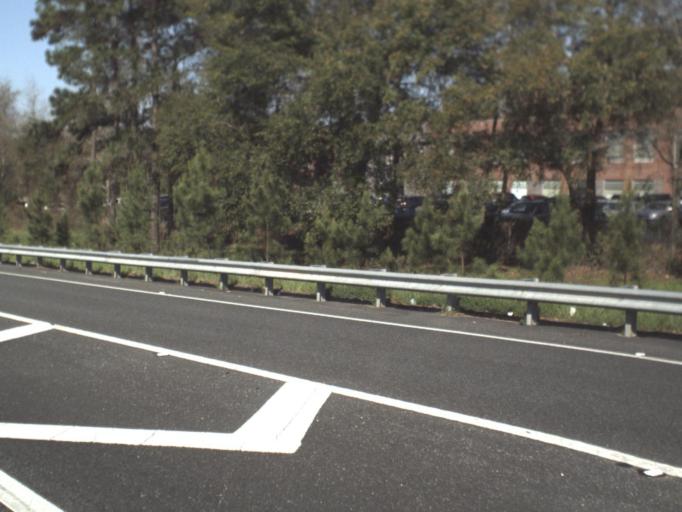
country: US
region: Florida
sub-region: Leon County
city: Tallahassee
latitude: 30.4814
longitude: -84.3151
